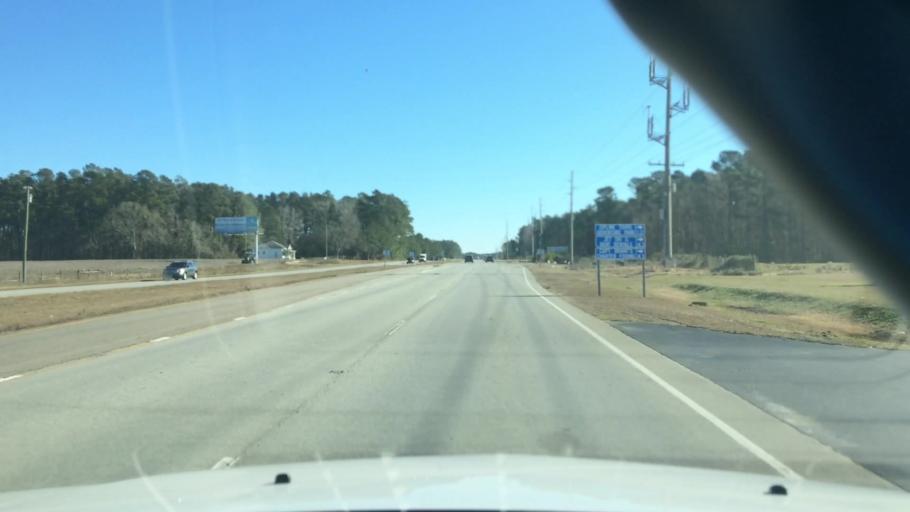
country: US
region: North Carolina
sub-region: Brunswick County
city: Shallotte
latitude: 33.9543
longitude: -78.4502
